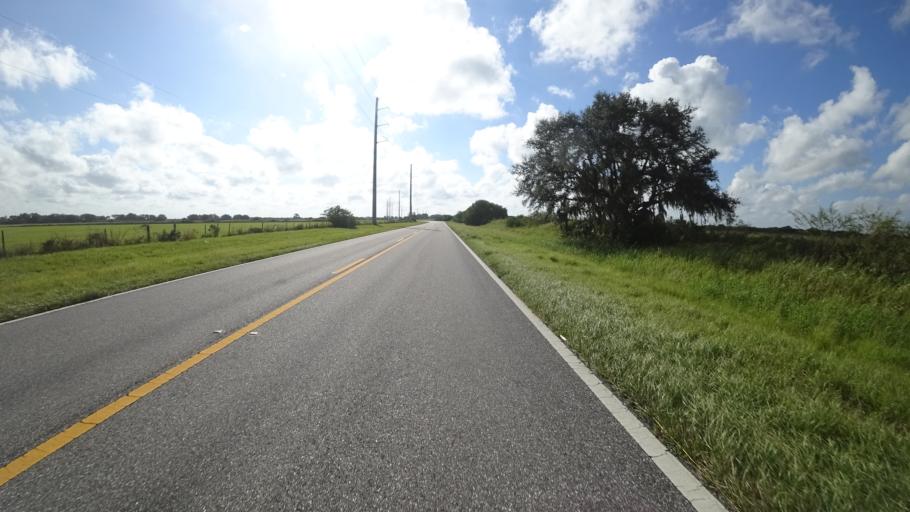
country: US
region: Florida
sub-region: Hillsborough County
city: Wimauma
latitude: 27.5172
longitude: -82.3260
